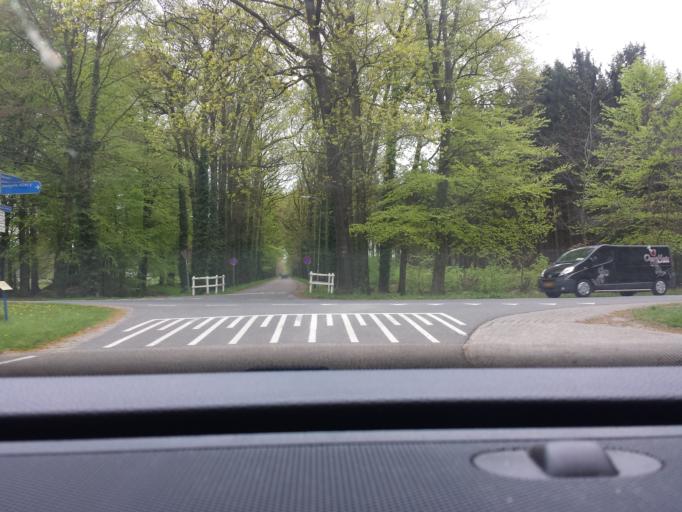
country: NL
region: Gelderland
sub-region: Gemeente Bronckhorst
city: Hengelo
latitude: 52.0702
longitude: 6.3740
